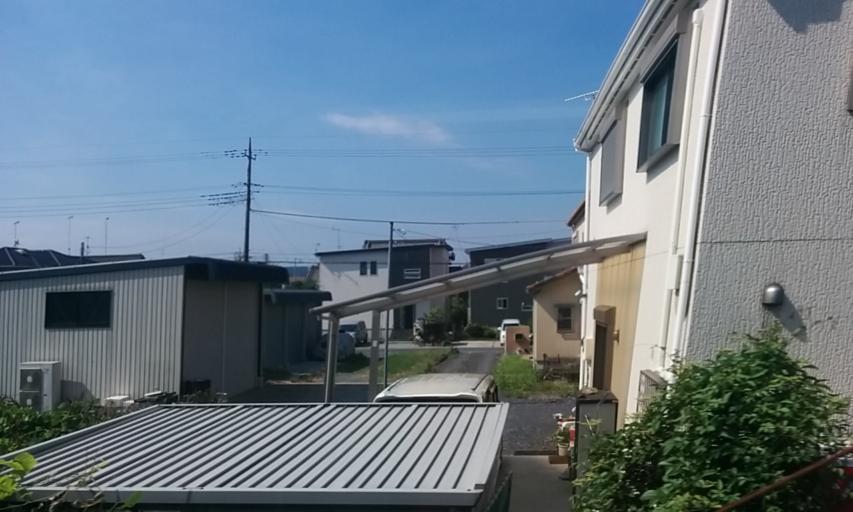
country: JP
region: Saitama
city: Kazo
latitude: 36.1182
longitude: 139.6088
